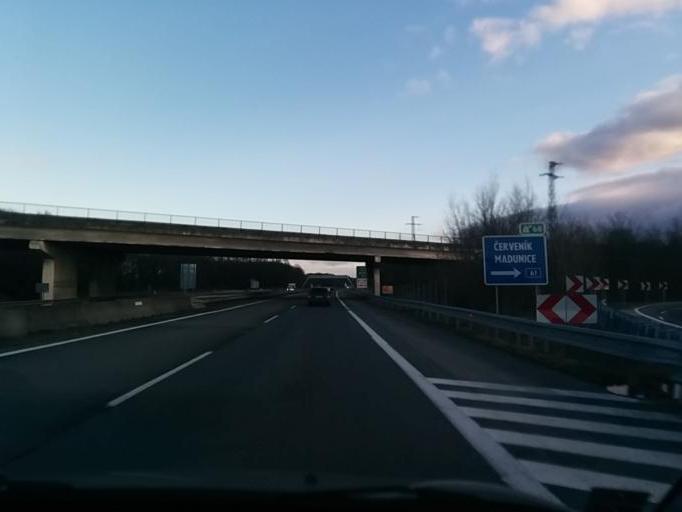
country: SK
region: Trnavsky
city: Leopoldov
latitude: 48.4582
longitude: 17.7395
